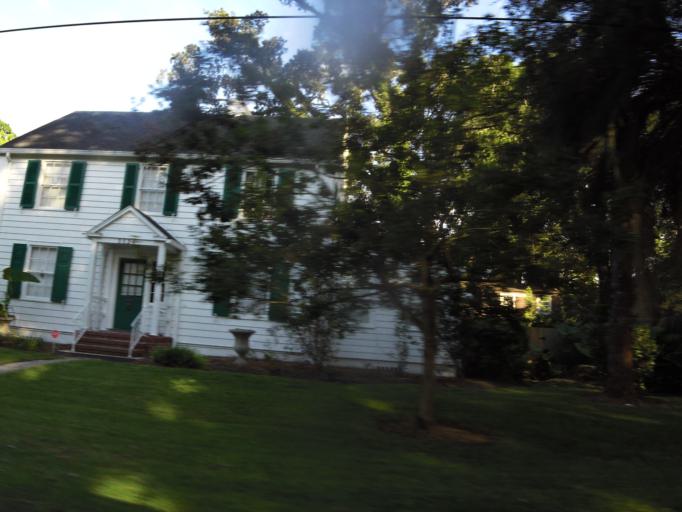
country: US
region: Florida
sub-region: Duval County
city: Jacksonville
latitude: 30.3048
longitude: -81.7108
